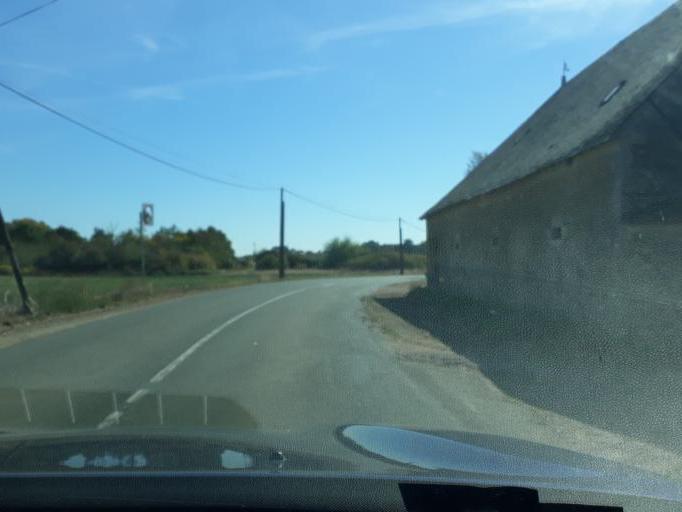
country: FR
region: Centre
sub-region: Departement du Loir-et-Cher
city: Ouzouer-le-Marche
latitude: 47.9271
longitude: 1.5200
